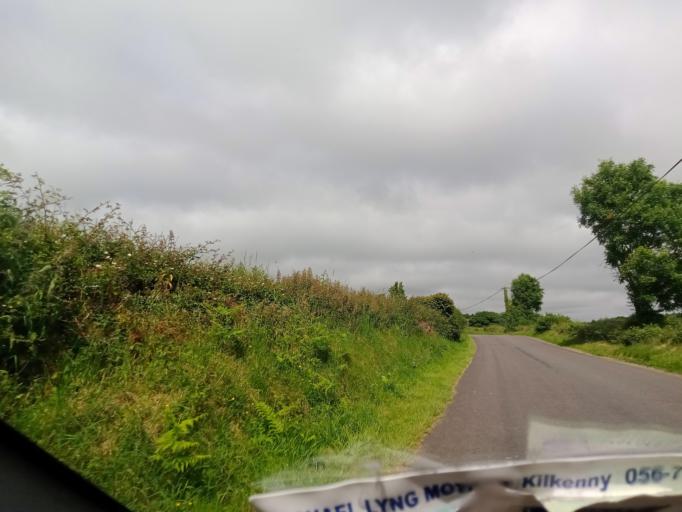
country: IE
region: Leinster
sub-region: Kilkenny
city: Ballyragget
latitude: 52.7657
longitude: -7.4675
